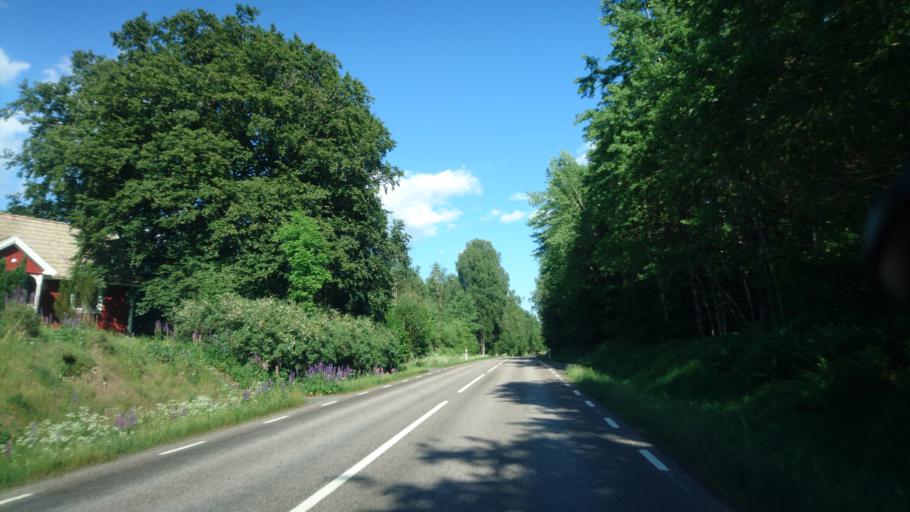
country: SE
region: Skane
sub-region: Osby Kommun
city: Lonsboda
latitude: 56.3913
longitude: 14.3458
